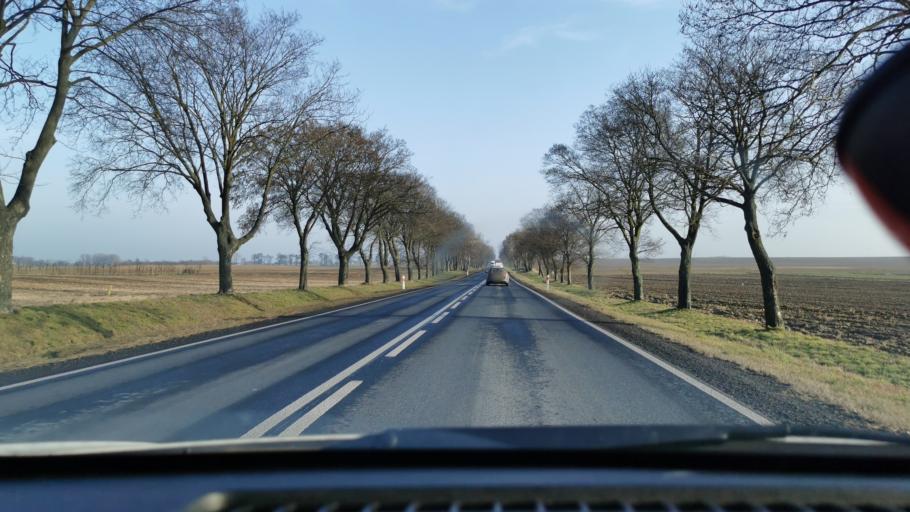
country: PL
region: Lodz Voivodeship
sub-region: Powiat sieradzki
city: Wroblew
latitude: 51.6235
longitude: 18.5749
